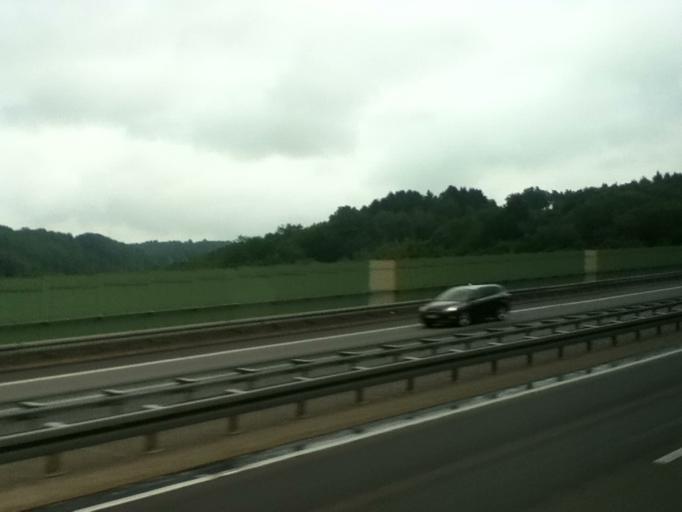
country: DE
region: North Rhine-Westphalia
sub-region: Regierungsbezirk Koln
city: Overath
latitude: 50.9429
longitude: 7.2323
